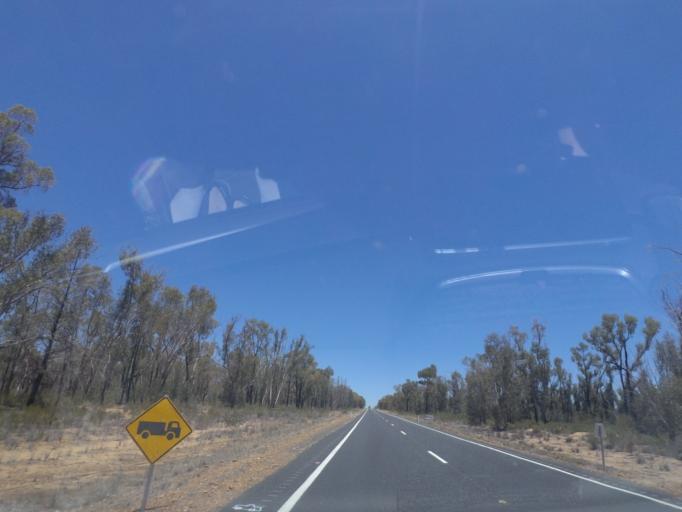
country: AU
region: New South Wales
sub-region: Warrumbungle Shire
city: Coonabarabran
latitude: -30.9573
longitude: 149.4203
